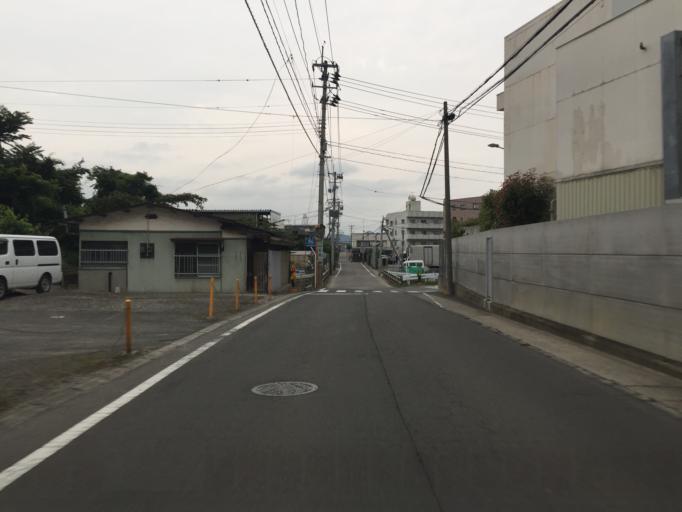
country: JP
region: Fukushima
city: Fukushima-shi
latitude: 37.7221
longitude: 140.4580
